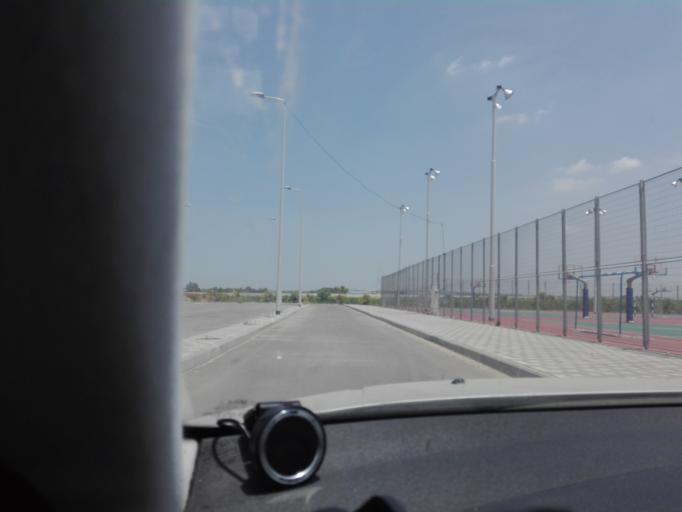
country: IL
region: Central District
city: Bene 'Ayish
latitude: 31.7421
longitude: 34.7427
